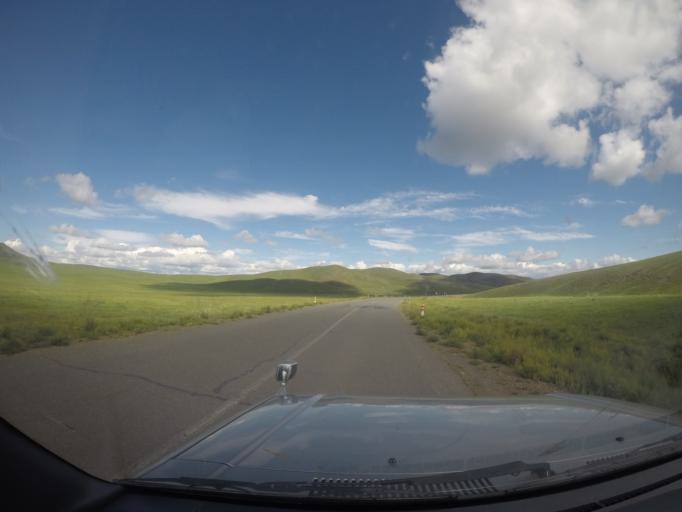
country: MN
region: Hentiy
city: Bayanbulag
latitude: 47.4566
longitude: 109.8191
